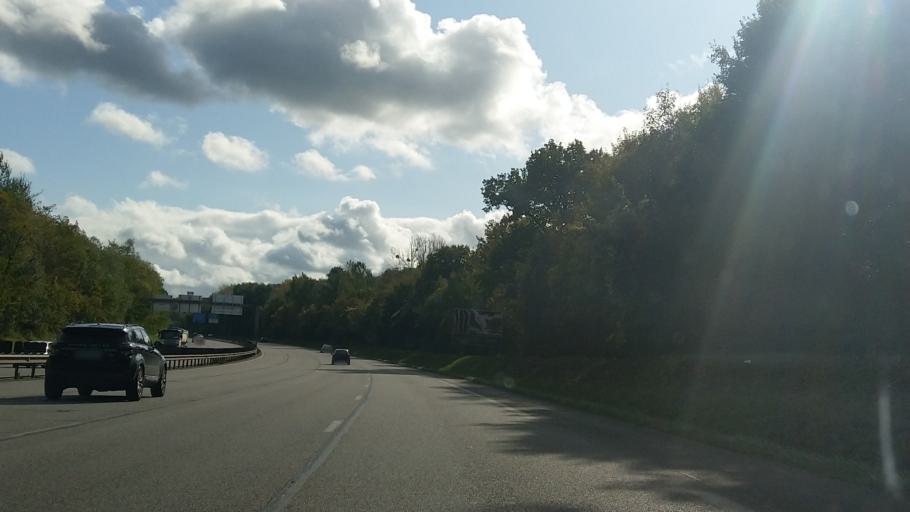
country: FR
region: Ile-de-France
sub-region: Departement du Val-d'Oise
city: Mours
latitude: 49.1181
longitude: 2.2525
